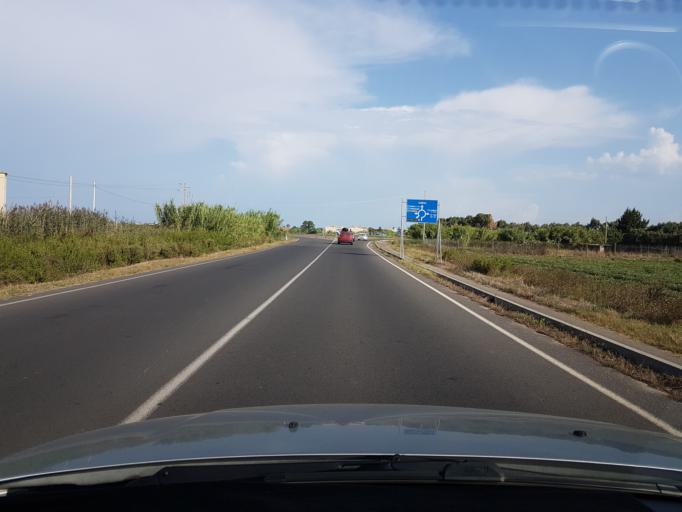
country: IT
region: Sardinia
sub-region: Provincia di Oristano
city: Cabras
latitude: 39.9181
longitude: 8.5388
